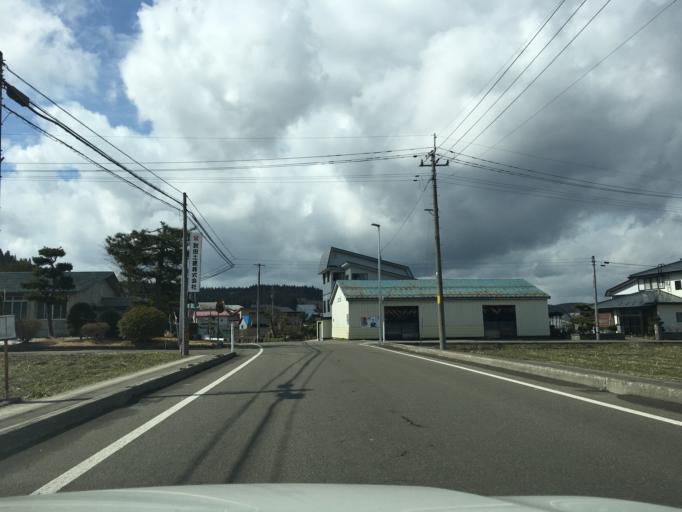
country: JP
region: Akita
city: Takanosu
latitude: 40.1197
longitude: 140.3727
